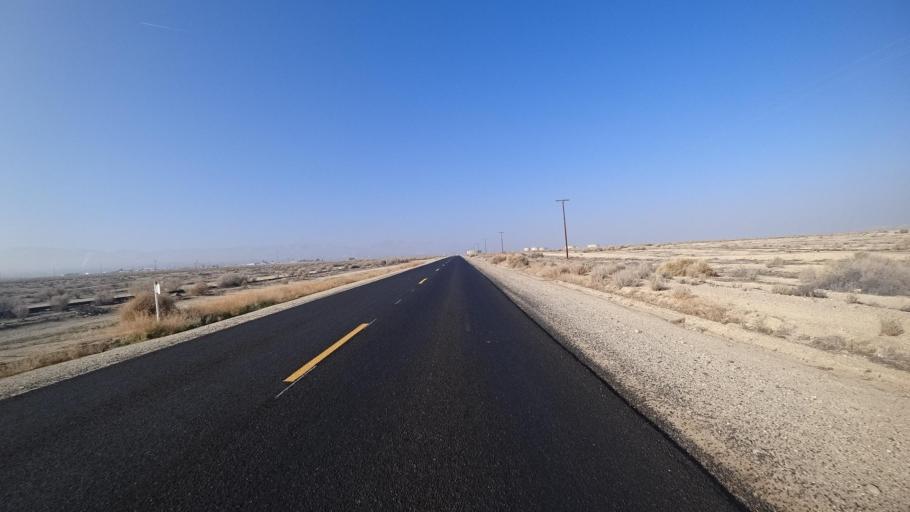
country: US
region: California
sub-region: Kern County
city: Ford City
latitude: 35.1805
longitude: -119.5062
